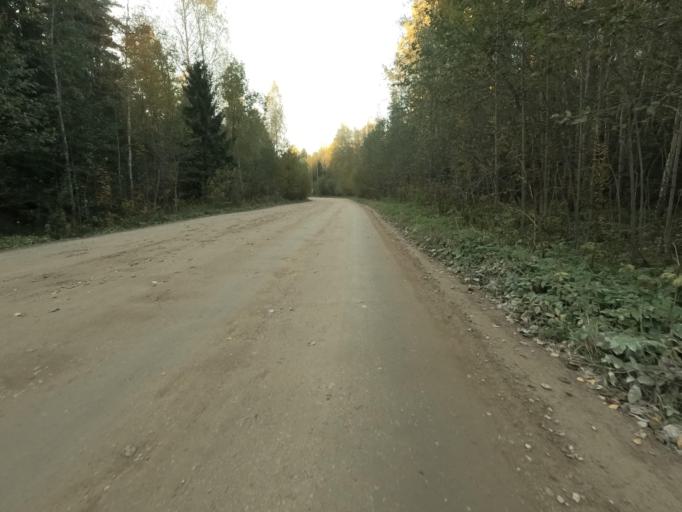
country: RU
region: Leningrad
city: Lyuban'
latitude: 59.0134
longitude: 31.0880
